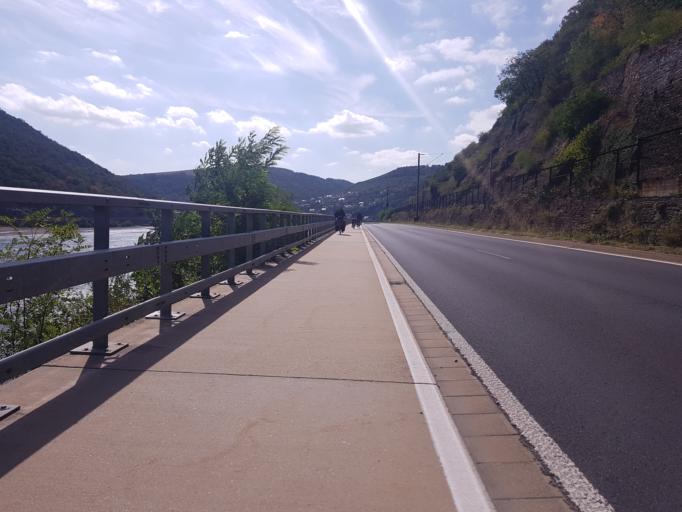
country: DE
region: Rheinland-Pfalz
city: Urbar
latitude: 50.1237
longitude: 7.7297
